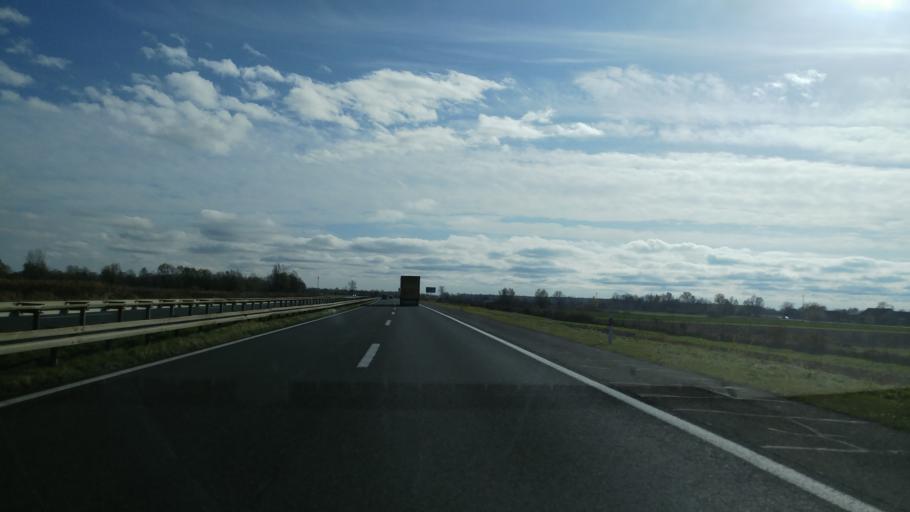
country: HR
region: Zagrebacka
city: Lupoglav
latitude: 45.7022
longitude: 16.3592
